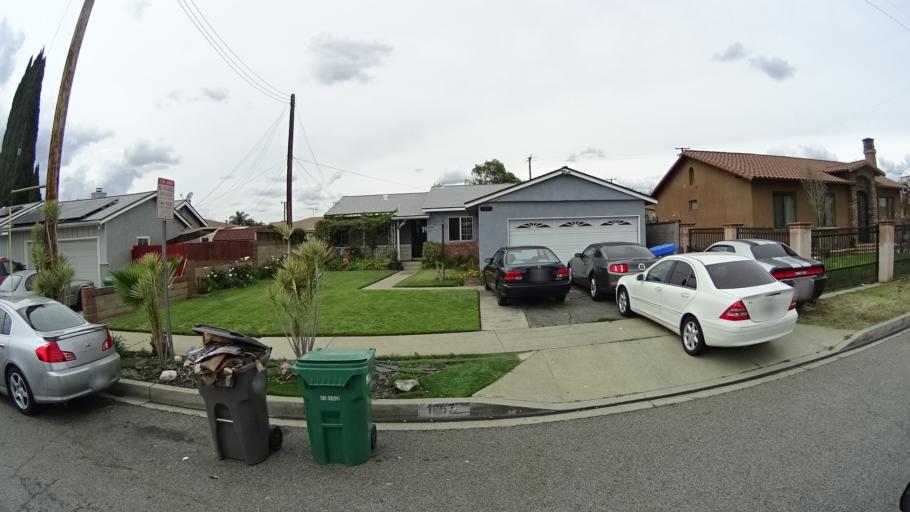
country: US
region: California
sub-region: Los Angeles County
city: West Puente Valley
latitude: 34.0670
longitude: -117.9620
